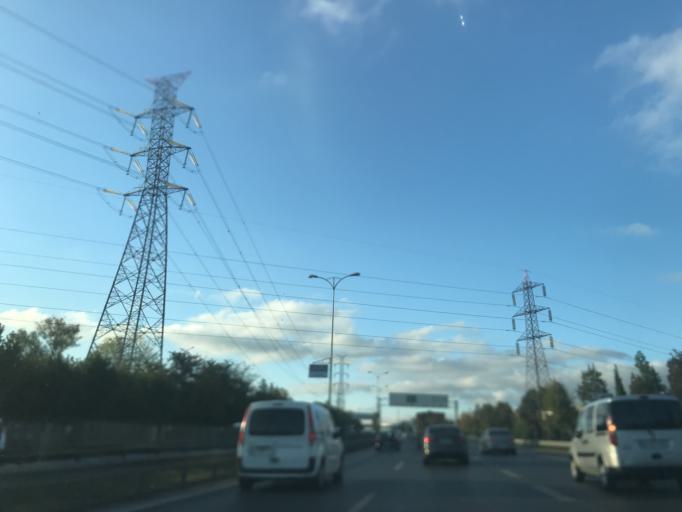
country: TR
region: Istanbul
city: Esenler
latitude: 41.0622
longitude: 28.8848
